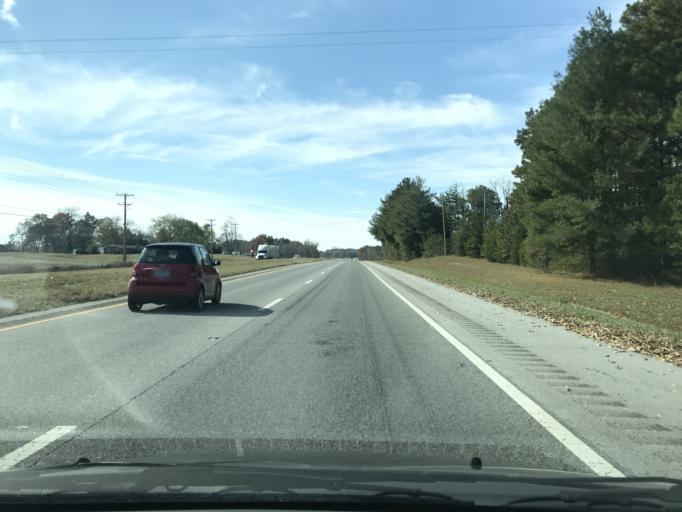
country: US
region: Tennessee
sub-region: Coffee County
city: Manchester
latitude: 35.4057
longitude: -86.1283
